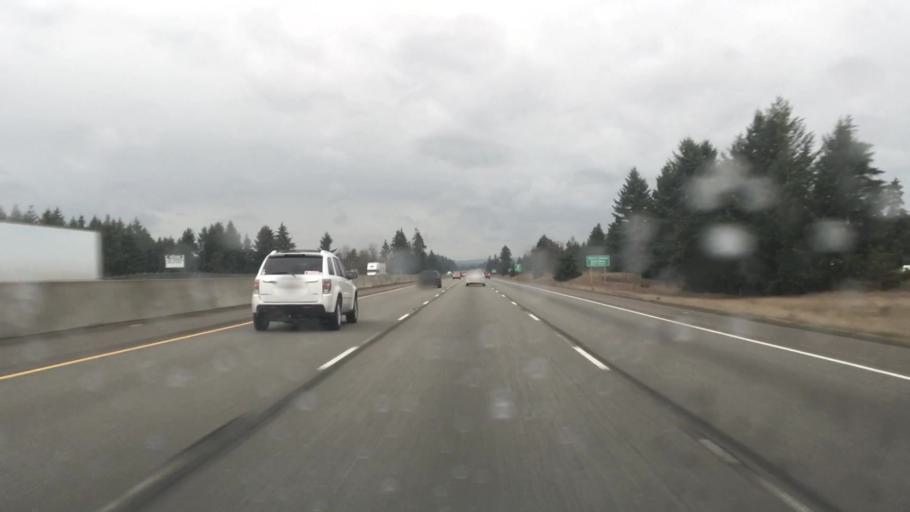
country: US
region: Washington
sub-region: Thurston County
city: Grand Mound
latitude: 46.8199
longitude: -122.9969
